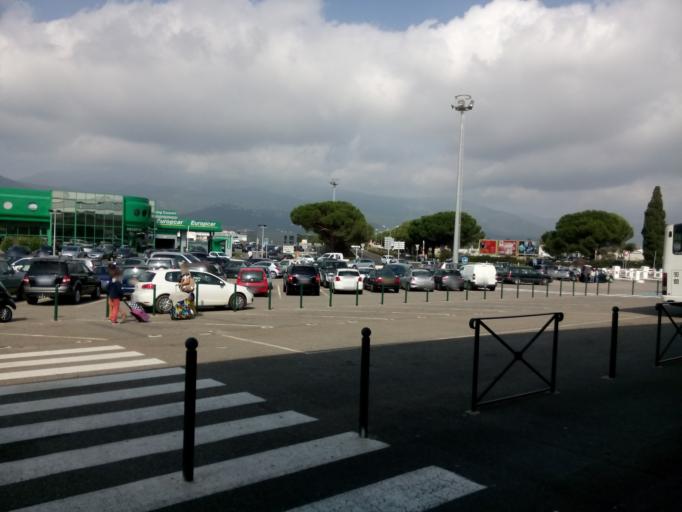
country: FR
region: Corsica
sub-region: Departement de la Haute-Corse
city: Borgo
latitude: 42.5472
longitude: 9.4801
